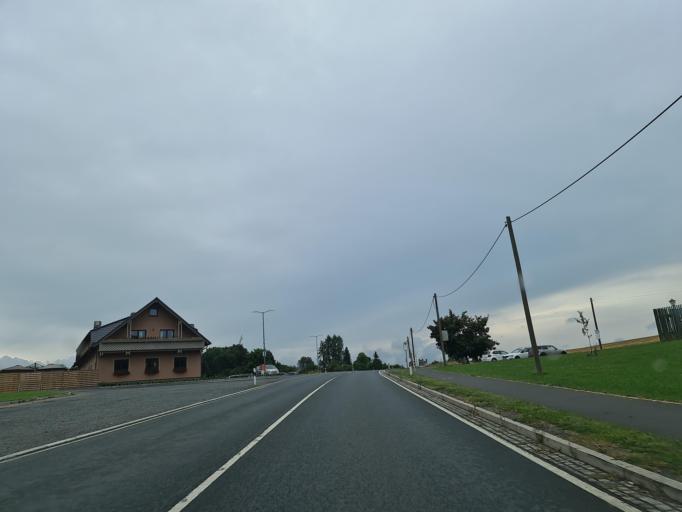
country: DE
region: Saxony
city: Oelsnitz
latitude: 50.4320
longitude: 12.1680
